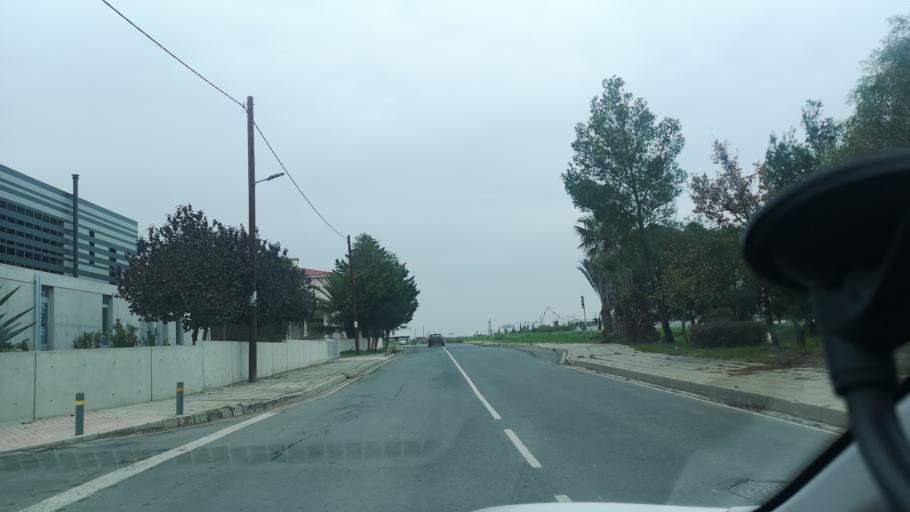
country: CY
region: Lefkosia
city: Tseri
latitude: 35.1079
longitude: 33.3536
